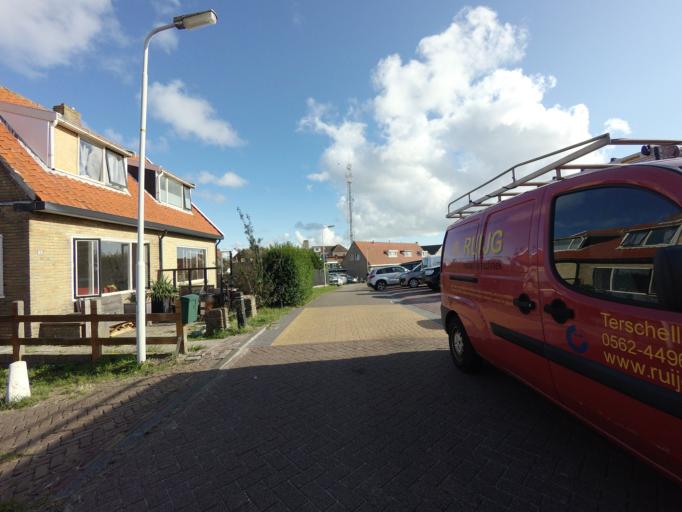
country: NL
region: Friesland
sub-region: Gemeente Terschelling
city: West-Terschelling
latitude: 53.3578
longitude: 5.2125
